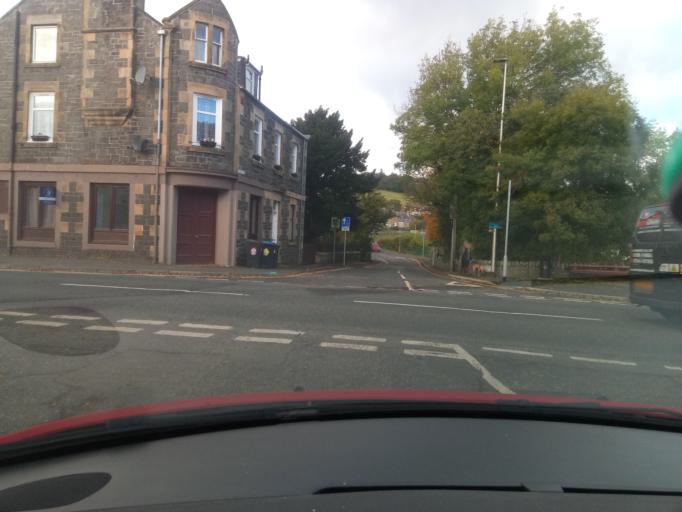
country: GB
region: Scotland
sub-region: The Scottish Borders
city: Galashiels
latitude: 55.6920
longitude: -2.8617
